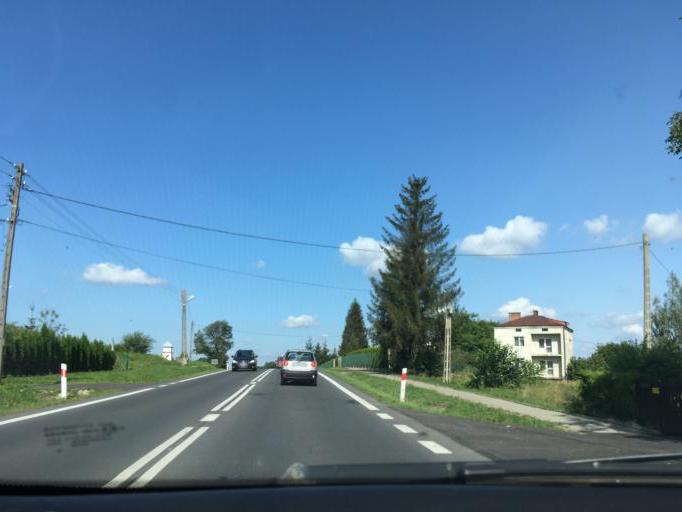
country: PL
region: Subcarpathian Voivodeship
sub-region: Powiat sanocki
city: Zagorz
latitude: 49.5211
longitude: 22.2556
